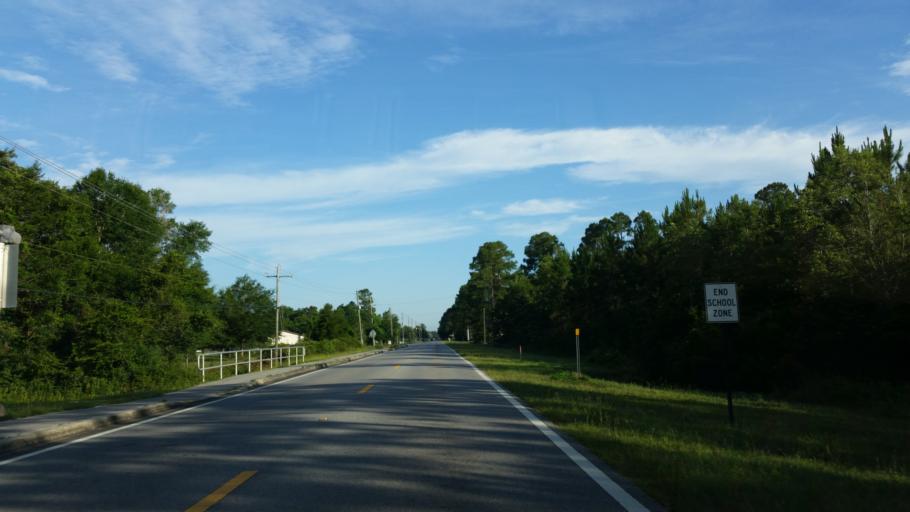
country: US
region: Florida
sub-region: Escambia County
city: Myrtle Grove
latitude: 30.3880
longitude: -87.3589
